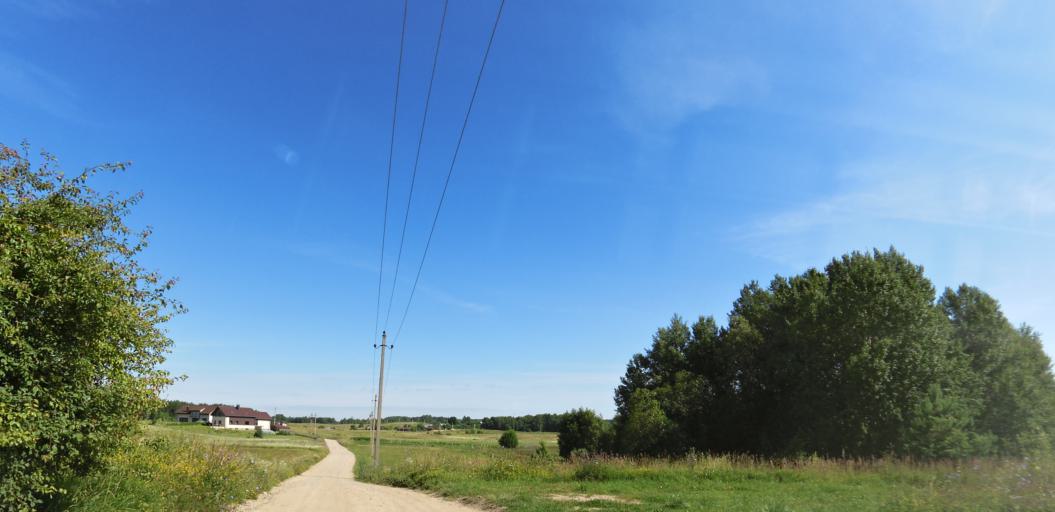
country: LT
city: Grigiskes
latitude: 54.7137
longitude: 25.0941
